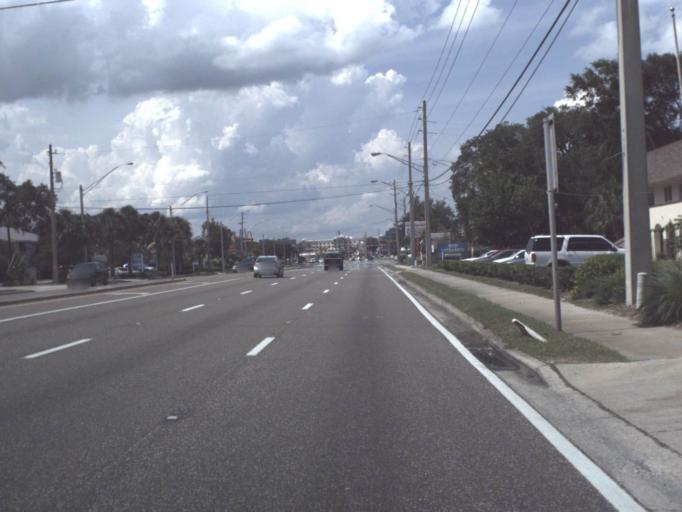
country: US
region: Florida
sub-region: Clay County
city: Orange Park
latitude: 30.1817
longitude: -81.7016
